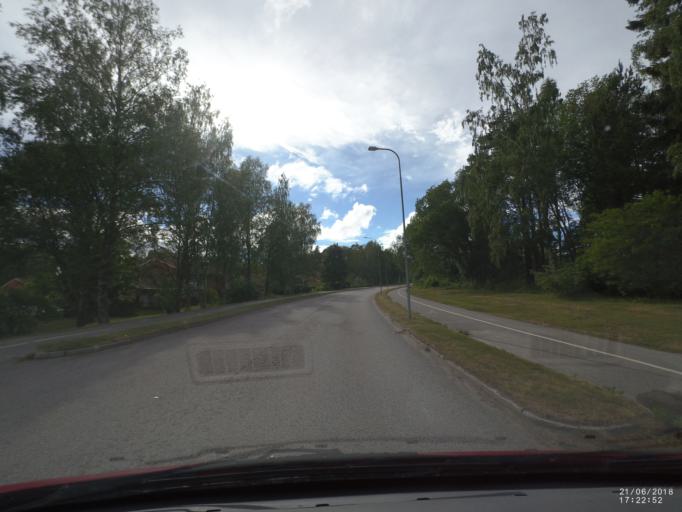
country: SE
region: Soedermanland
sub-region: Nykopings Kommun
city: Nykoping
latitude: 58.7518
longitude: 17.0607
